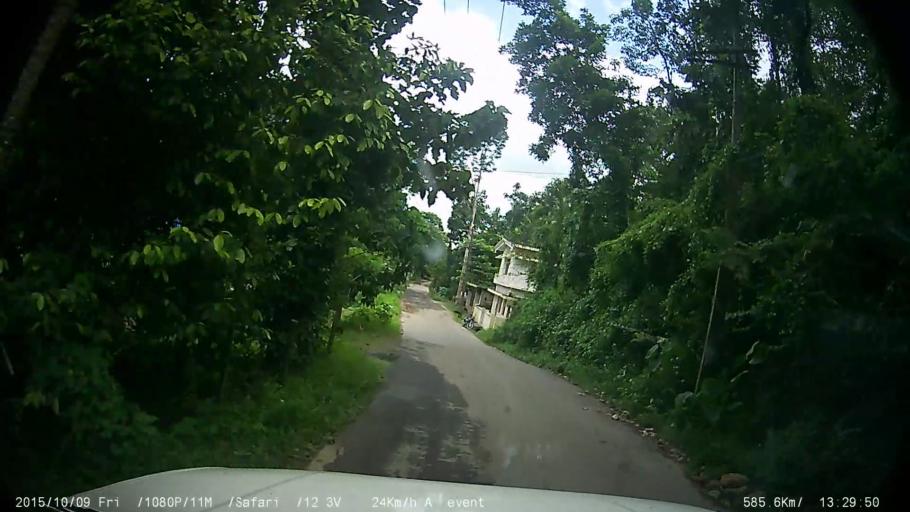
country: IN
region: Kerala
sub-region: Ernakulam
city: Ramamangalam
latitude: 9.9166
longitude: 76.5533
